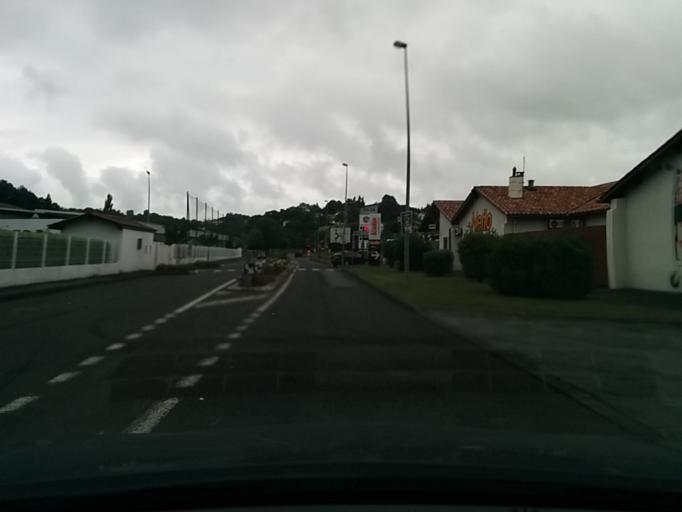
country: FR
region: Aquitaine
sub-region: Departement des Pyrenees-Atlantiques
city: Saint-Pee-sur-Nivelle
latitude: 43.3529
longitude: -1.5499
